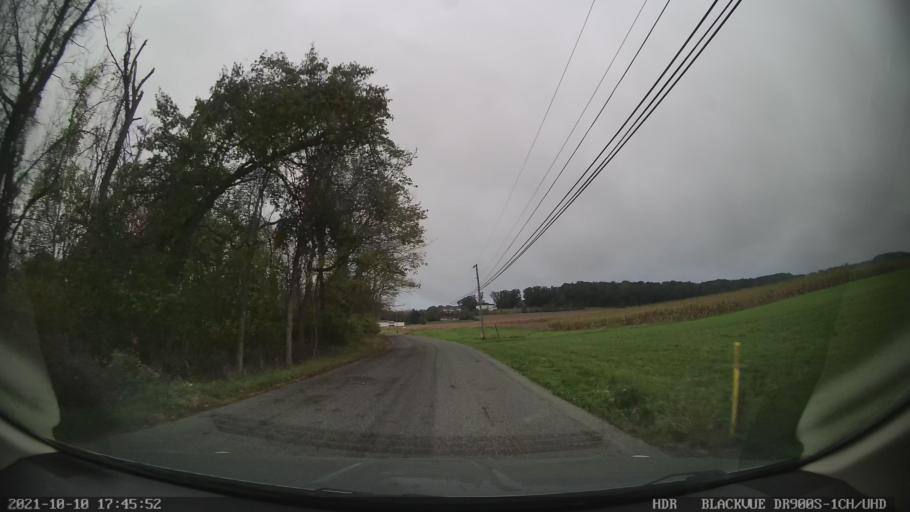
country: US
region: Pennsylvania
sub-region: Lehigh County
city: Breinigsville
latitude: 40.5560
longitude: -75.6755
